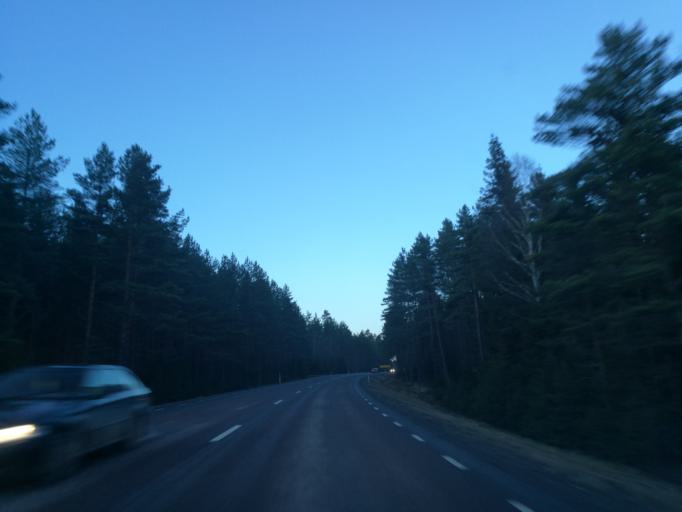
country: SE
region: Vaermland
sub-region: Eda Kommun
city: Charlottenberg
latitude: 59.8969
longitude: 12.2788
